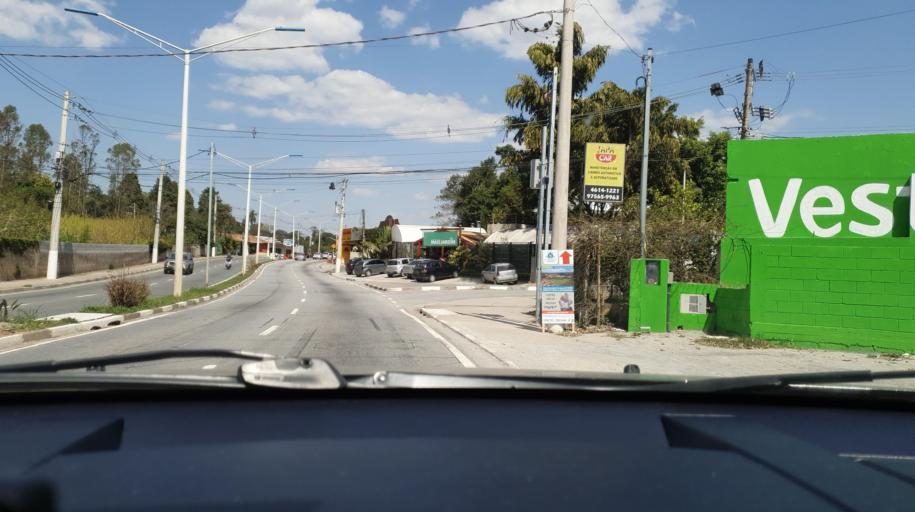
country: BR
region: Sao Paulo
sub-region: Vargem Grande Paulista
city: Vargem Grande Paulista
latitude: -23.6184
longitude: -46.9738
